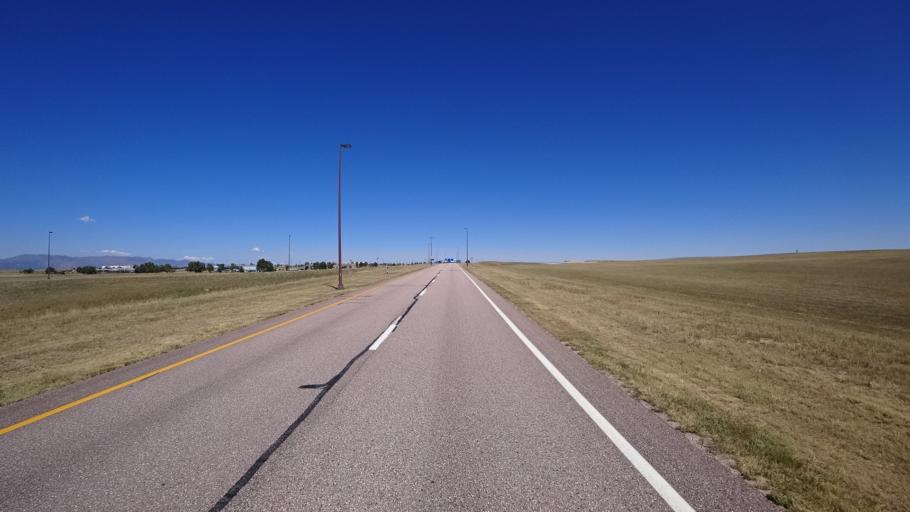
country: US
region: Colorado
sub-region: El Paso County
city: Security-Widefield
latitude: 38.7877
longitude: -104.6974
